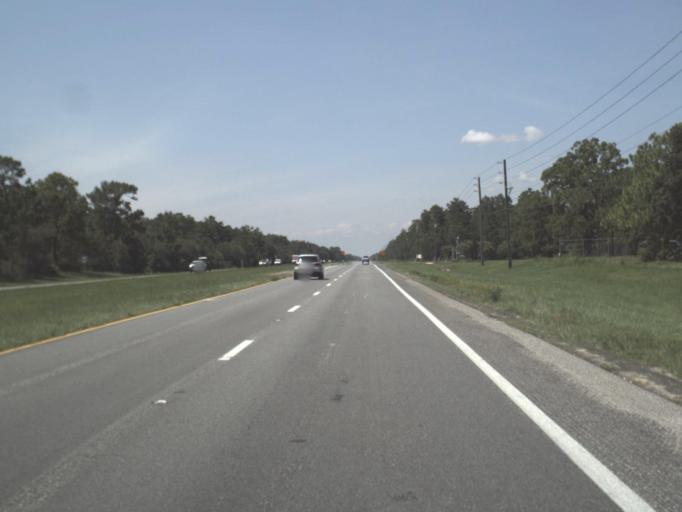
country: US
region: Florida
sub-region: Hernando County
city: North Weeki Wachee
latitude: 28.6036
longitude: -82.5516
